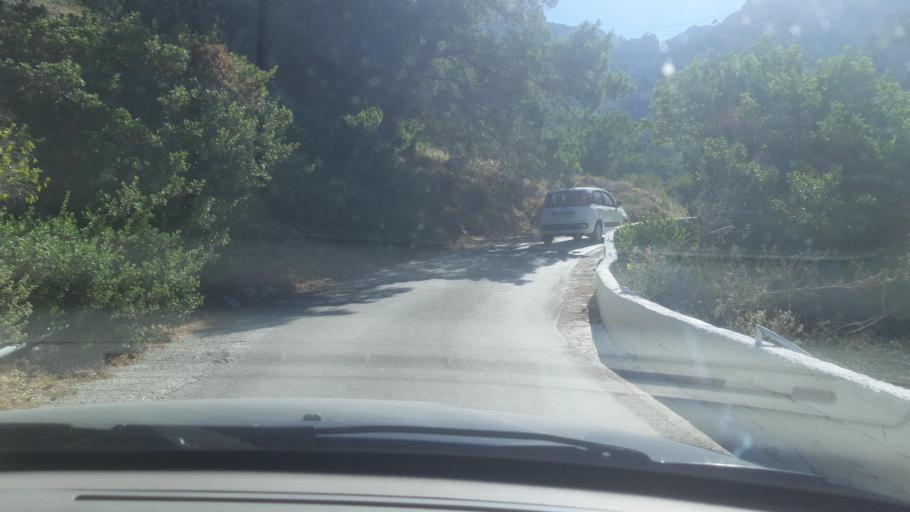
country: GR
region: South Aegean
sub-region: Nomos Dodekanisou
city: Karpathos
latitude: 35.5854
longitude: 27.1770
